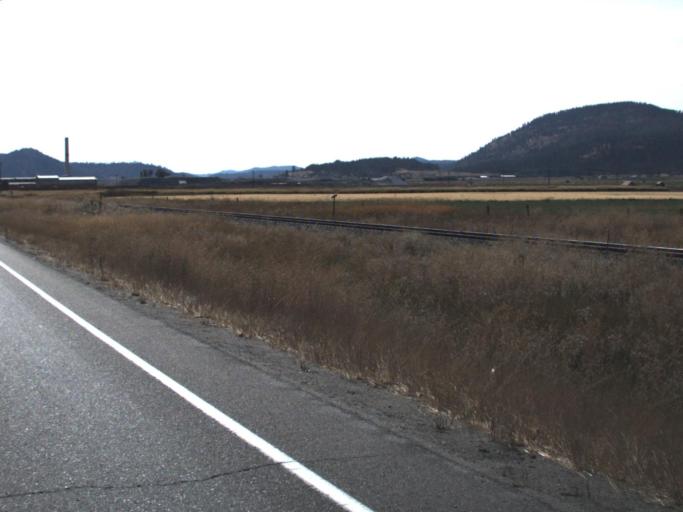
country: US
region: Washington
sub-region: Stevens County
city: Chewelah
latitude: 48.2632
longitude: -117.7154
